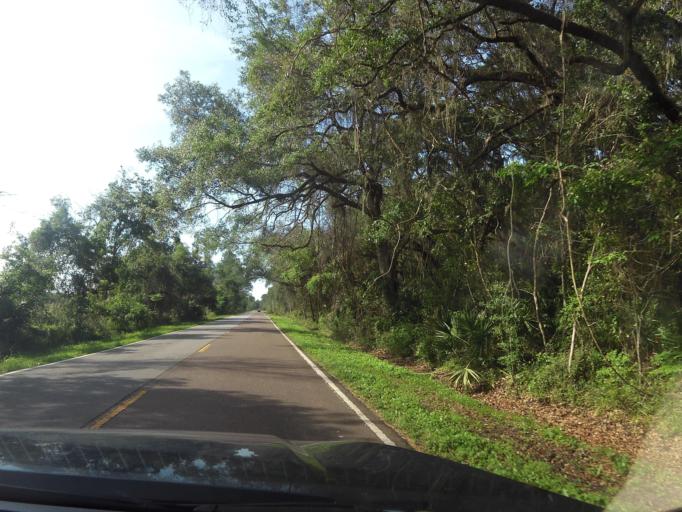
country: US
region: Florida
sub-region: Nassau County
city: Fernandina Beach
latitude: 30.5035
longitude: -81.4737
